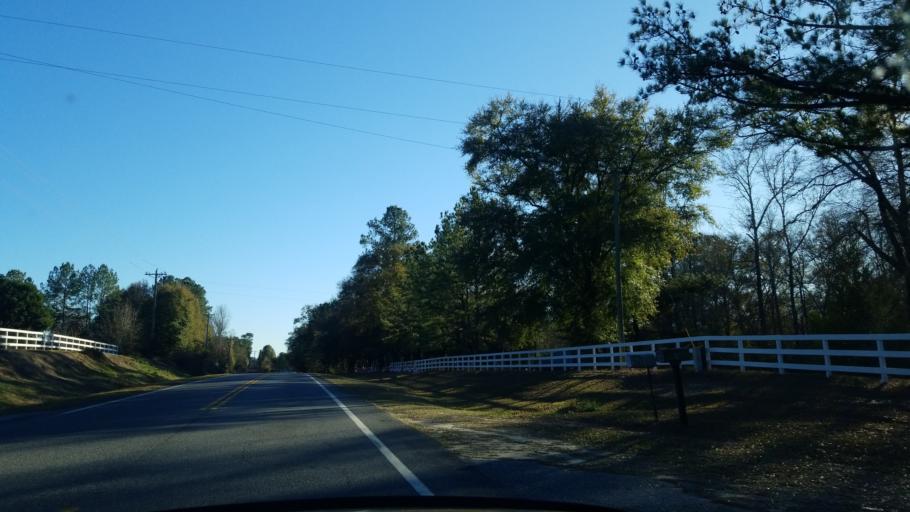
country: US
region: Georgia
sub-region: Talbot County
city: Talbotton
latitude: 32.5592
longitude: -84.6045
